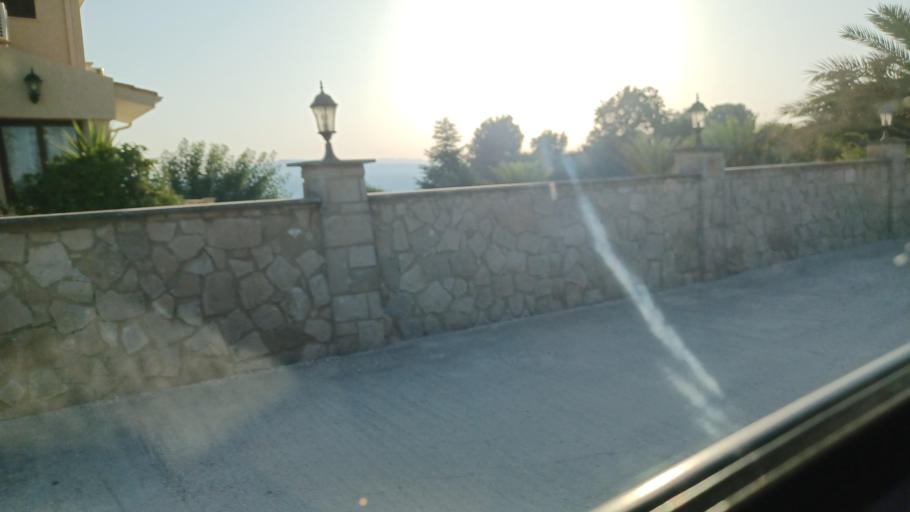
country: CY
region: Pafos
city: Mesogi
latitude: 34.8567
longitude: 32.4922
